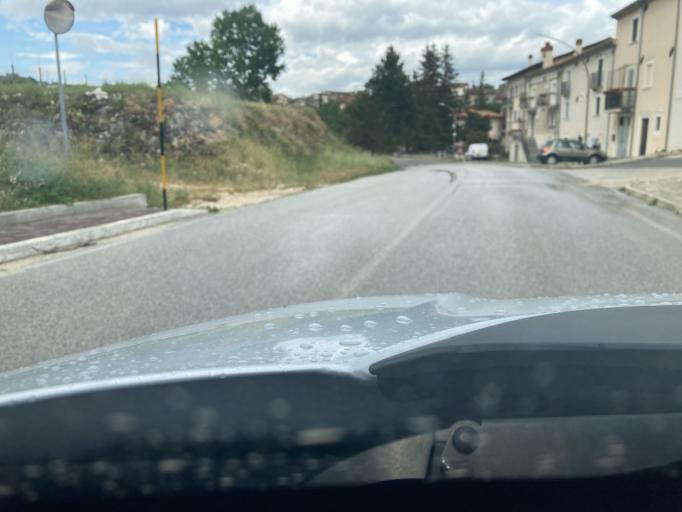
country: IT
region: Abruzzo
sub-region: Provincia dell' Aquila
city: Rocca di Mezzo
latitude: 42.2329
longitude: 13.5346
